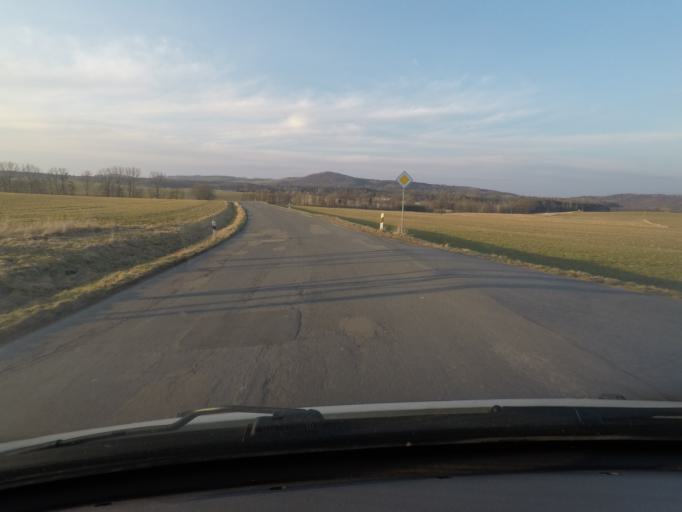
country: DE
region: Saxony
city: Reinhardtsgrimma
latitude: 50.8978
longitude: 13.7495
